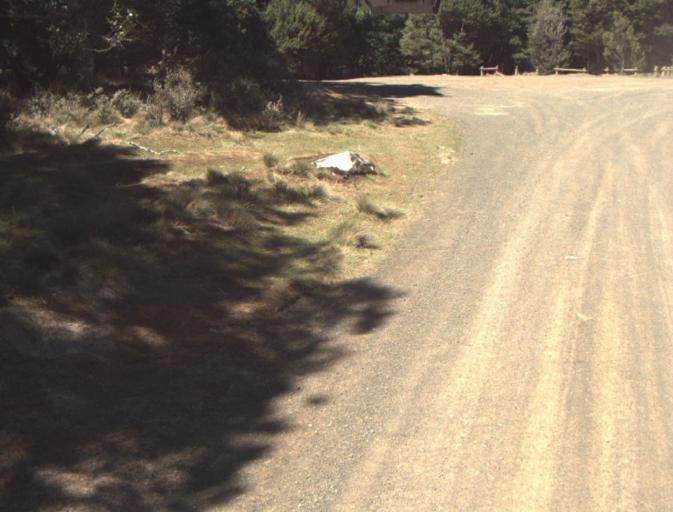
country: AU
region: Tasmania
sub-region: Dorset
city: Scottsdale
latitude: -41.3676
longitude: 147.4306
